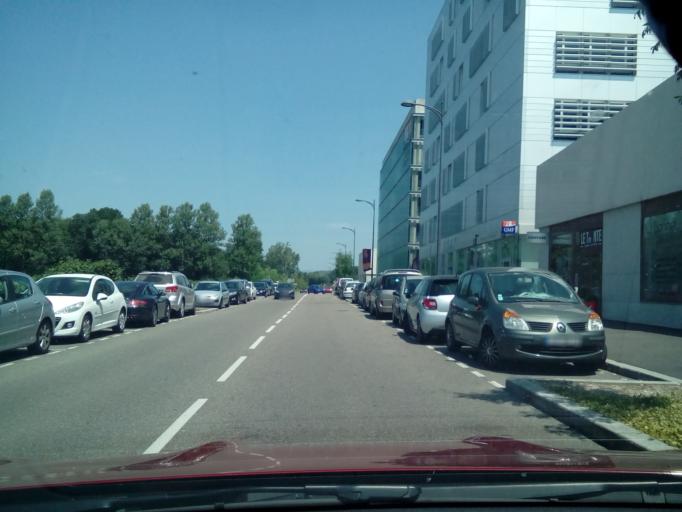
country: FR
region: Rhone-Alpes
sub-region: Departement de l'Isere
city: Domarin
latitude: 45.5972
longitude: 5.2425
